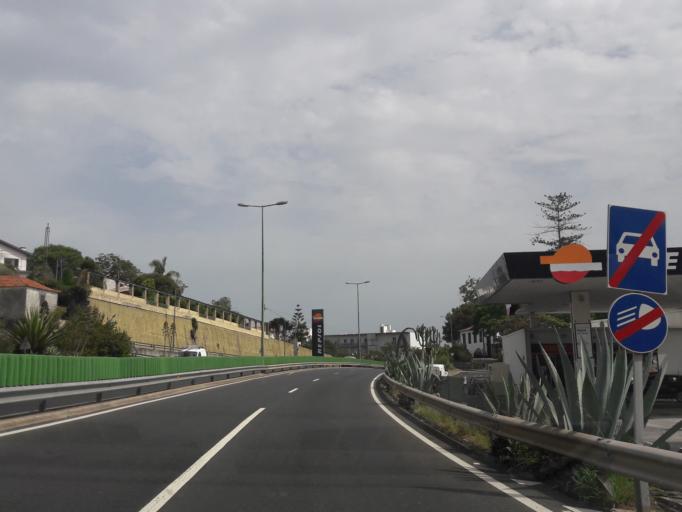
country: PT
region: Madeira
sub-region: Funchal
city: Nossa Senhora do Monte
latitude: 32.6520
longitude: -16.9262
